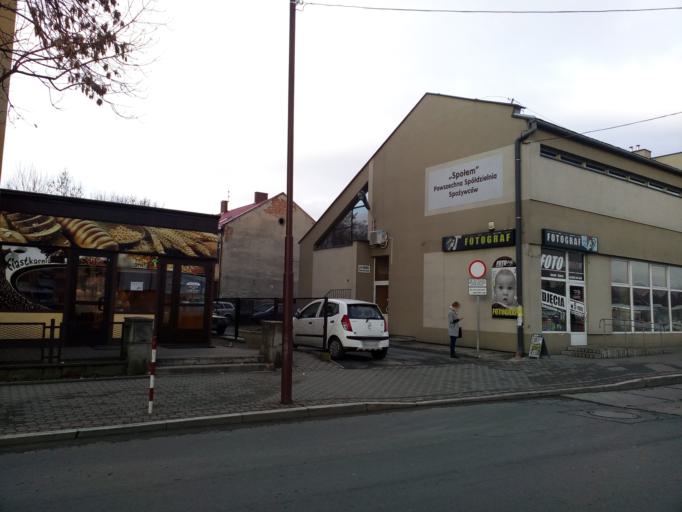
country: PL
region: Lesser Poland Voivodeship
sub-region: Powiat nowosadecki
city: Nowy Sacz
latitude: 49.6171
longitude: 20.6974
